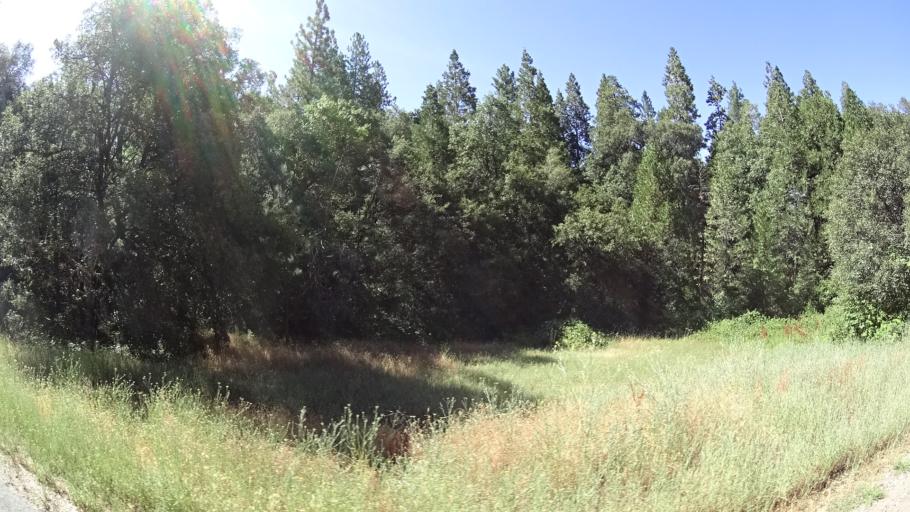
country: US
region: California
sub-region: Amador County
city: Pioneer
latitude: 38.3960
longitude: -120.4793
